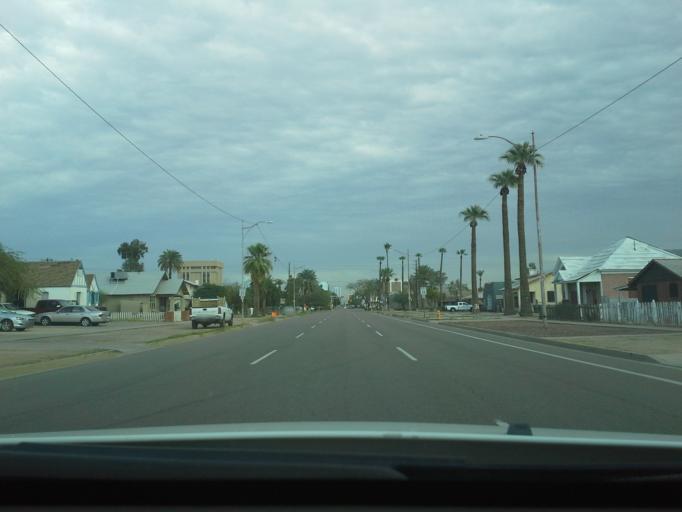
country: US
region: Arizona
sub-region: Maricopa County
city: Phoenix
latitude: 33.4470
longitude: -112.1041
